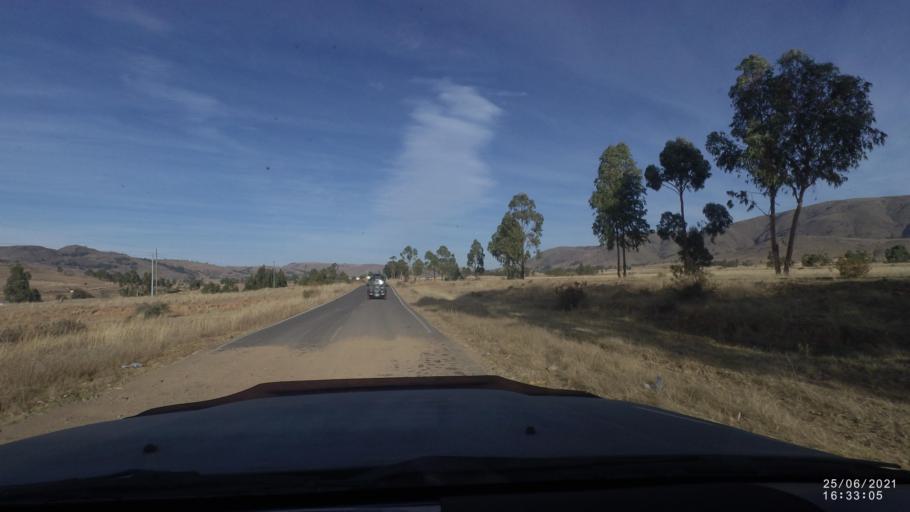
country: BO
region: Cochabamba
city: Arani
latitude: -17.8111
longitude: -65.7888
